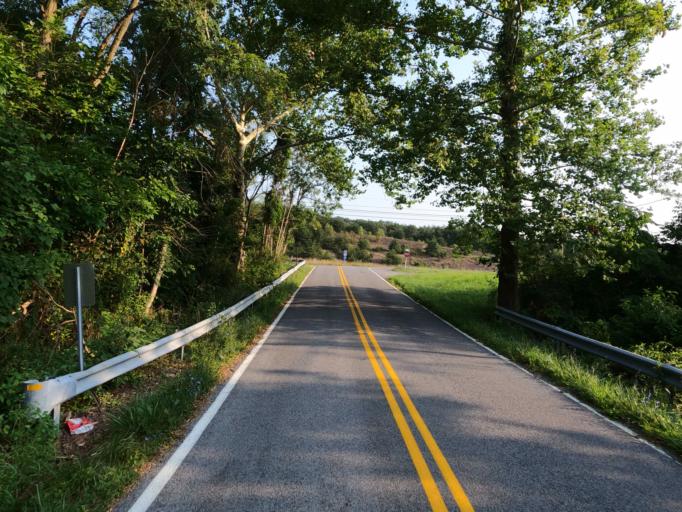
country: US
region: Maryland
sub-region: Washington County
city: Hancock
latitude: 39.6970
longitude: -78.2445
